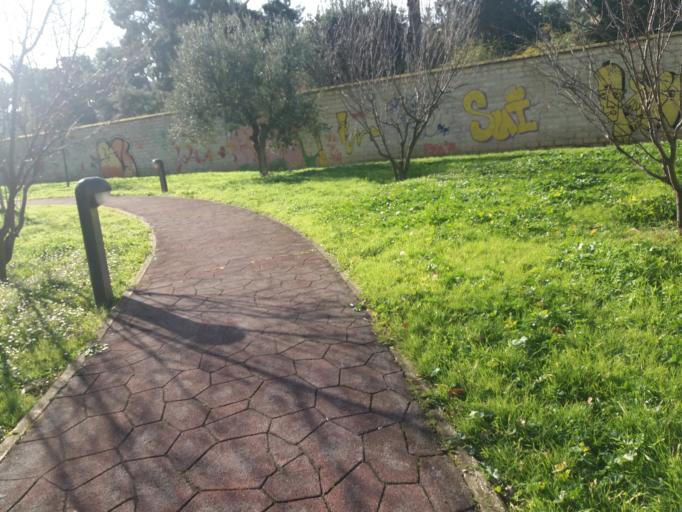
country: IT
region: Apulia
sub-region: Provincia di Barletta - Andria - Trani
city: Andria
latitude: 41.2351
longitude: 16.3049
